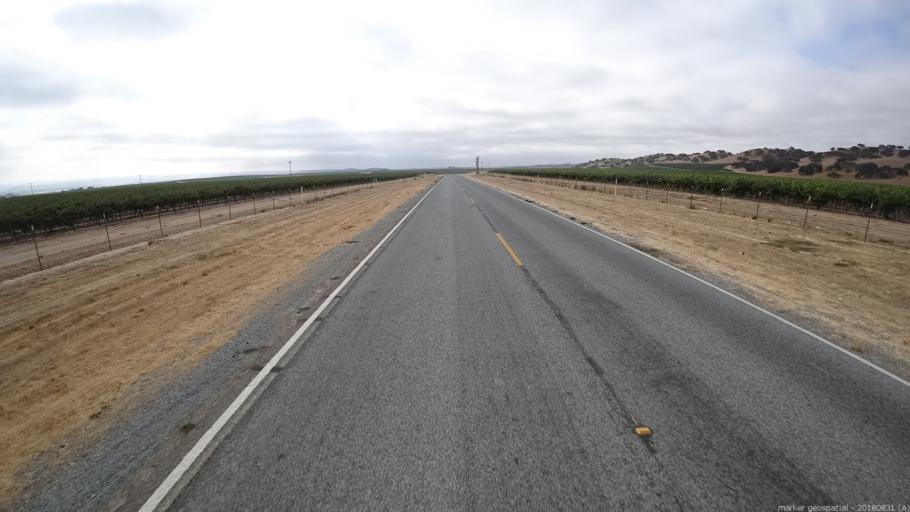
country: US
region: California
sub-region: Monterey County
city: King City
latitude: 36.1854
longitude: -121.1390
